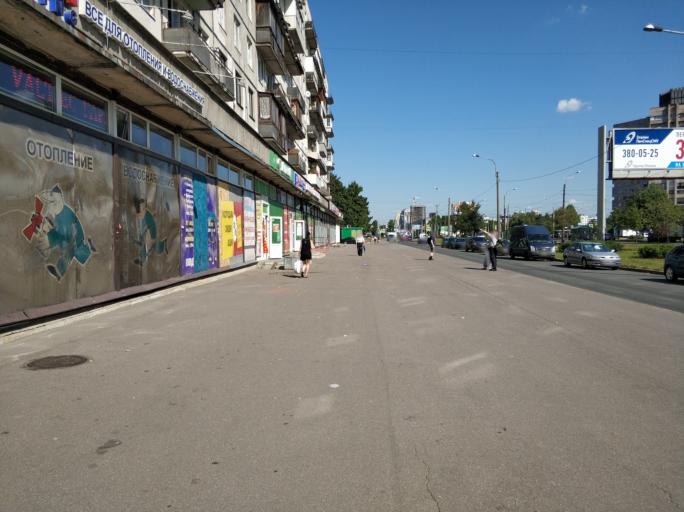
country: RU
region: Leningrad
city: Akademicheskoe
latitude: 60.0195
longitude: 30.4034
